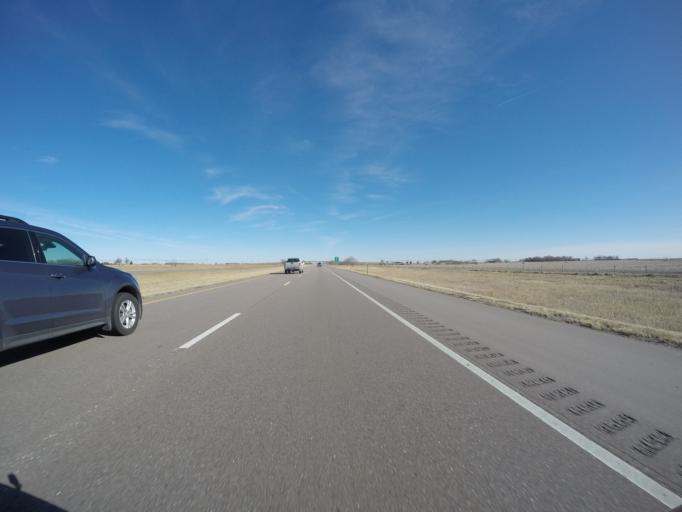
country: US
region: Nebraska
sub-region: York County
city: York
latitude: 40.8211
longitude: -97.6244
